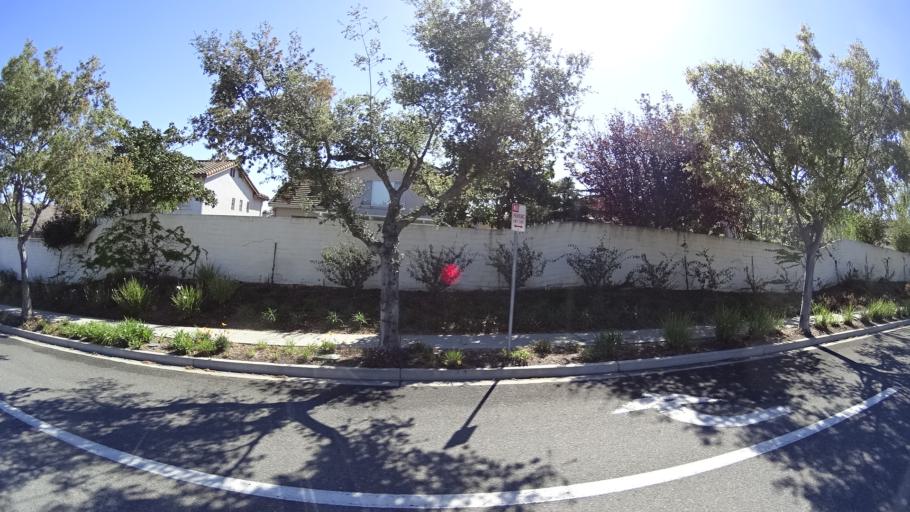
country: US
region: California
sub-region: Ventura County
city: Casa Conejo
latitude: 34.1658
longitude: -118.9721
